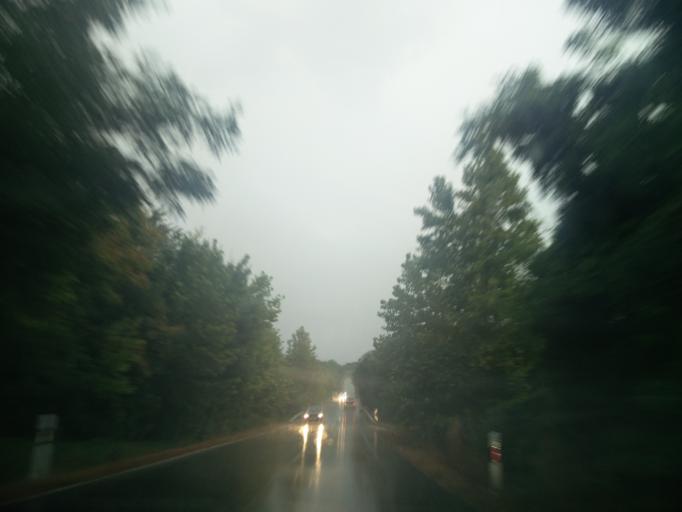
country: HU
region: Pest
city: Biatorbagy
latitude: 47.4579
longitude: 18.7906
